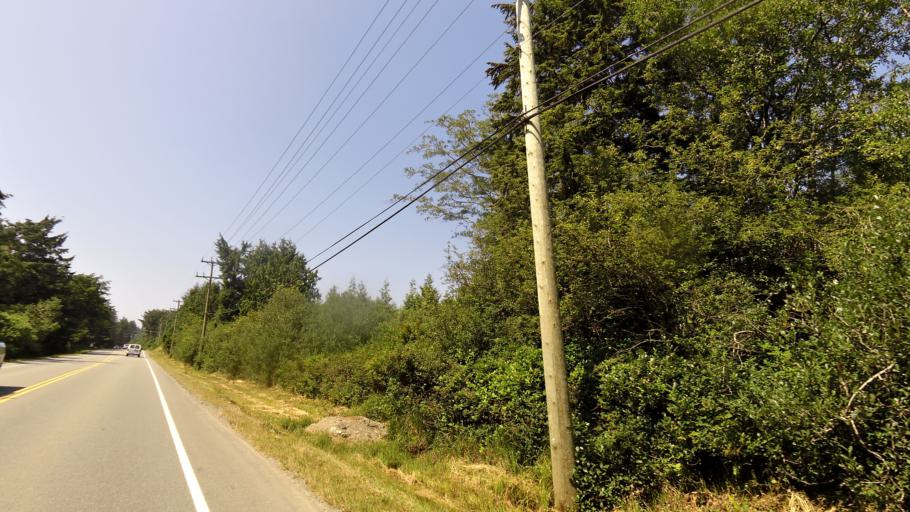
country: CA
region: British Columbia
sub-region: Regional District of Alberni-Clayoquot
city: Tofino
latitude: 49.0729
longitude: -125.7618
